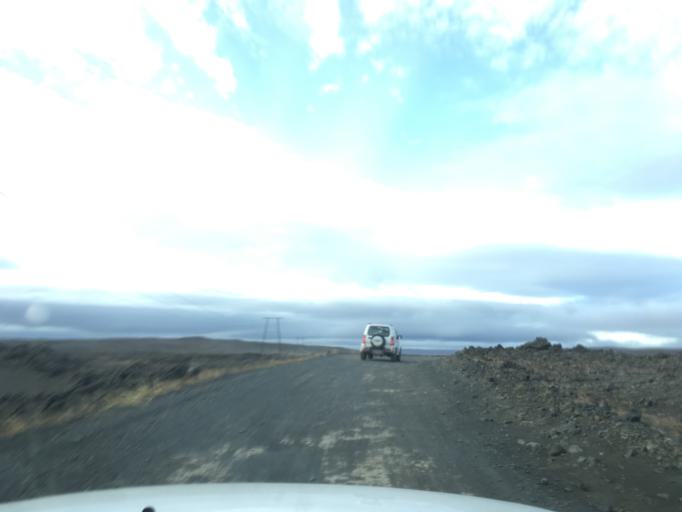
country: IS
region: South
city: Vestmannaeyjar
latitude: 64.1410
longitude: -19.1285
